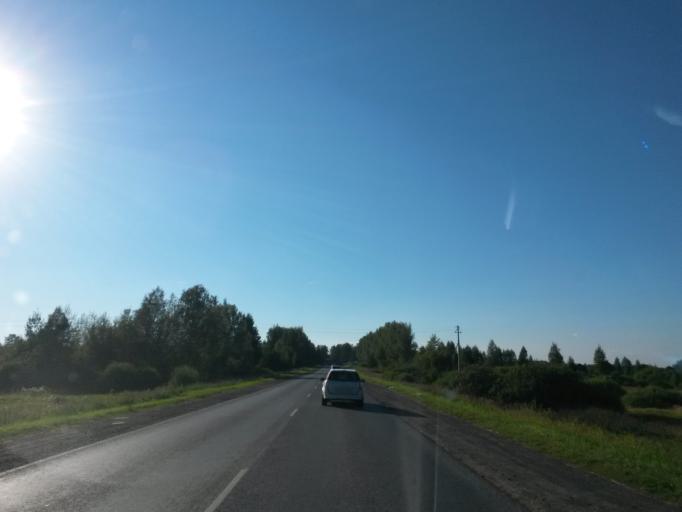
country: RU
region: Ivanovo
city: Novo-Talitsy
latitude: 57.0235
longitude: 40.7656
